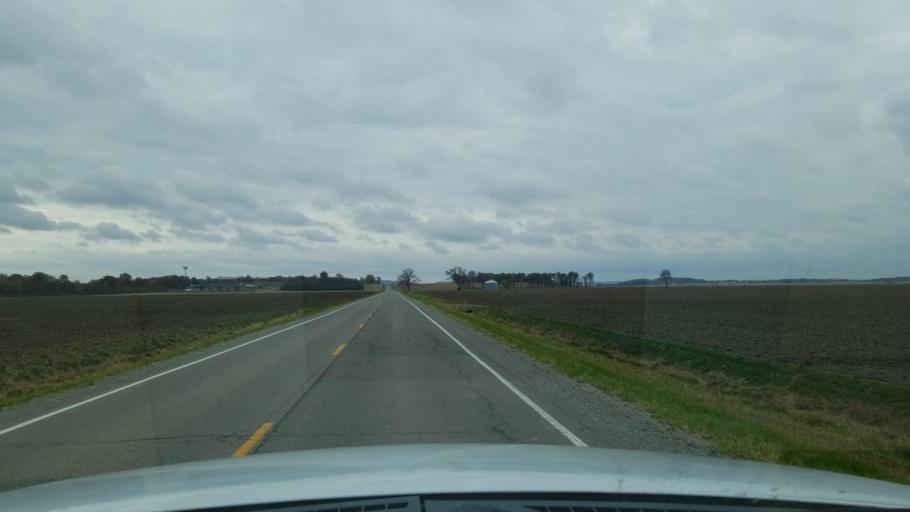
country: US
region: Illinois
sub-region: Saline County
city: Eldorado
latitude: 37.7658
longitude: -88.4383
